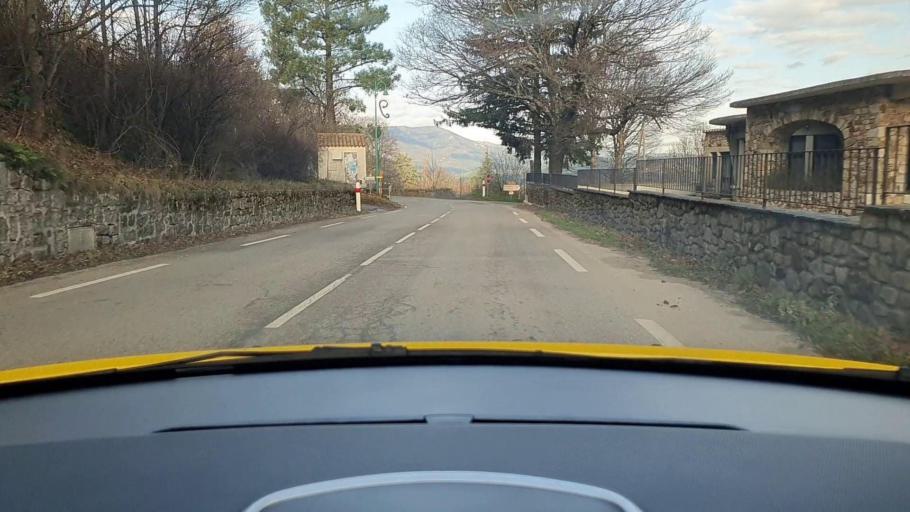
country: FR
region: Languedoc-Roussillon
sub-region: Departement du Gard
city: Branoux-les-Taillades
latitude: 44.2682
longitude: 4.0248
